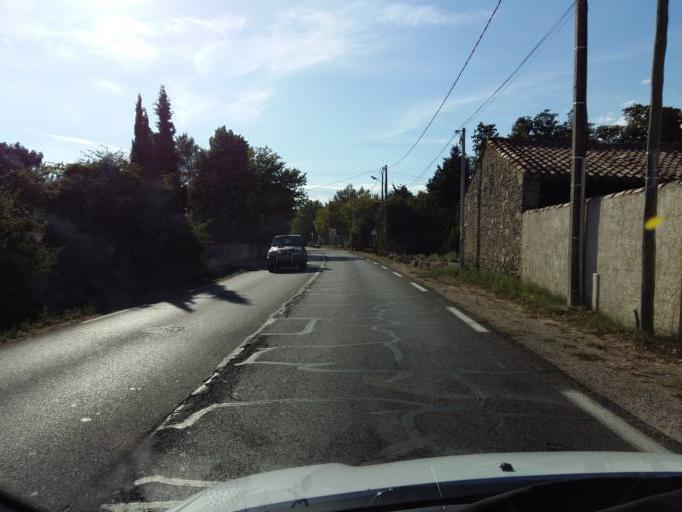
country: FR
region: Provence-Alpes-Cote d'Azur
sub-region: Departement du Vaucluse
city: Chateauneuf-de-Gadagne
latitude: 43.9268
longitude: 4.9535
